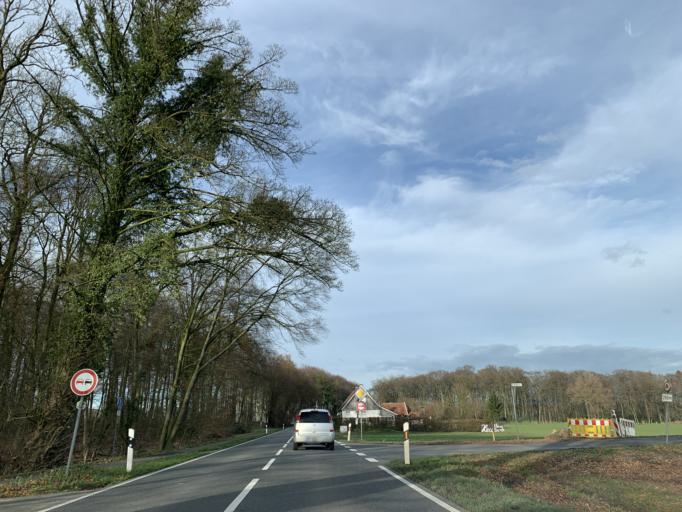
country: DE
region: North Rhine-Westphalia
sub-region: Regierungsbezirk Munster
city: Nottuln
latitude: 51.9395
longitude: 7.3351
